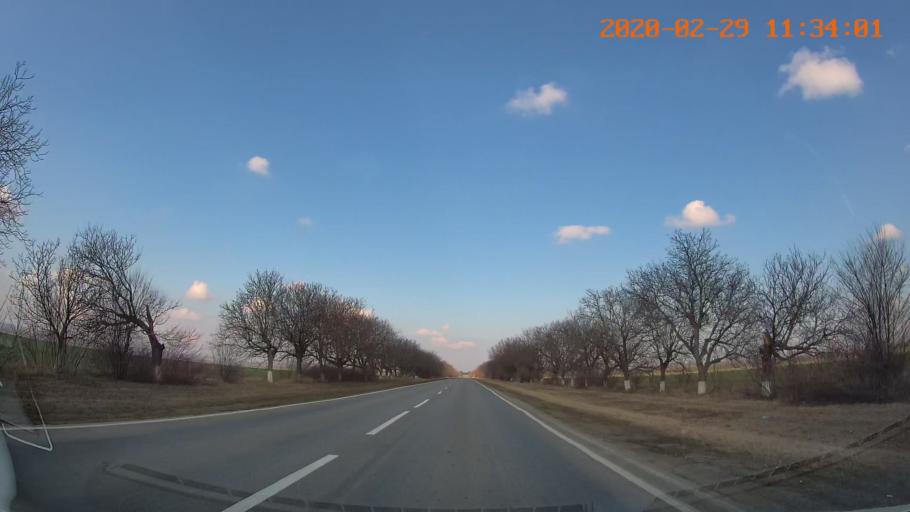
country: MD
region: Rezina
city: Saharna
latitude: 47.5596
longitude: 29.0784
